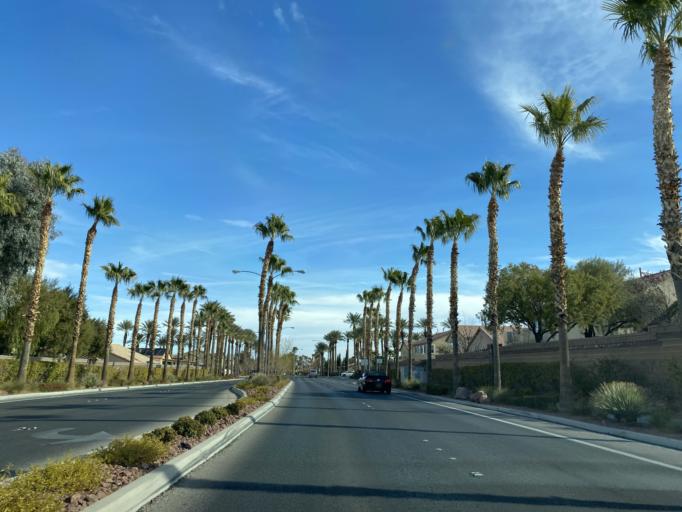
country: US
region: Nevada
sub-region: Clark County
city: Enterprise
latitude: 36.0479
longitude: -115.2530
